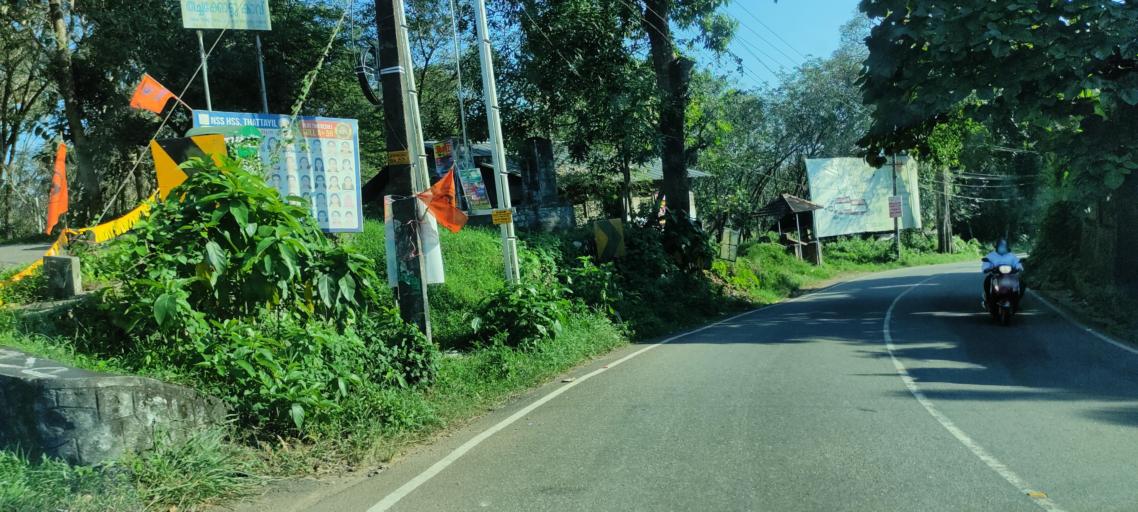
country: IN
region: Kerala
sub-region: Pattanamtitta
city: Adur
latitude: 9.1938
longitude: 76.7455
